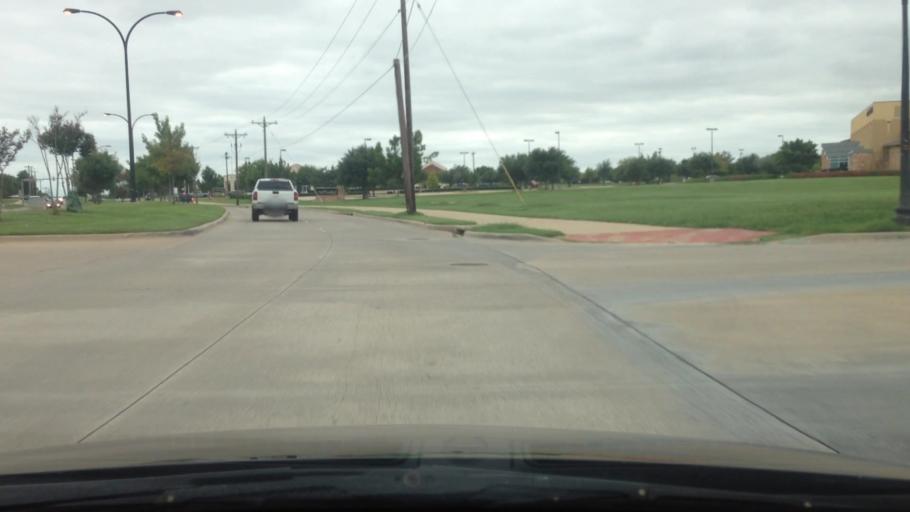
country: US
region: Texas
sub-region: Tarrant County
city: Keller
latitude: 32.9013
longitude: -97.2385
